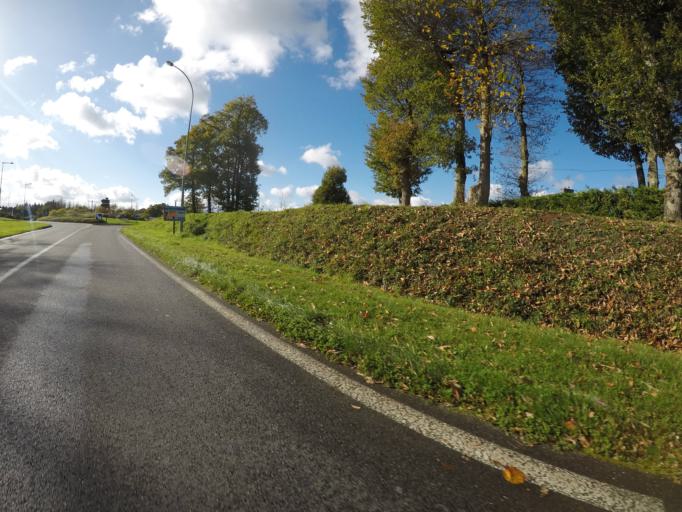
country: FR
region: Brittany
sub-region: Departement des Cotes-d'Armor
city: Bourbriac
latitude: 48.4857
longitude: -3.1863
